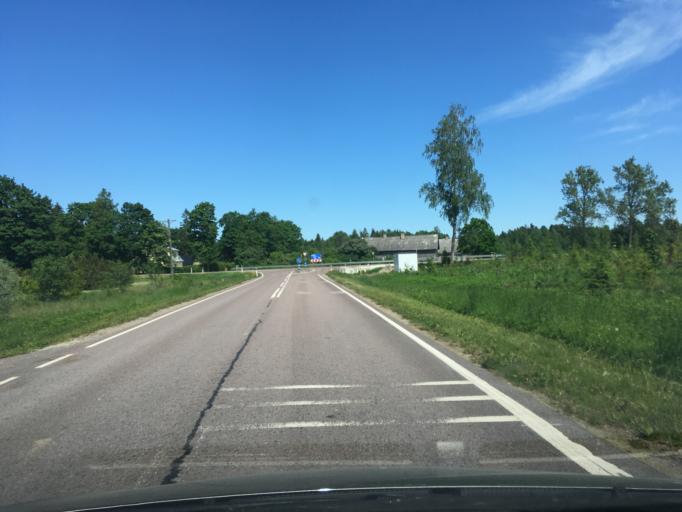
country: EE
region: Raplamaa
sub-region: Rapla vald
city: Rapla
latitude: 59.0675
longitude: 24.9139
